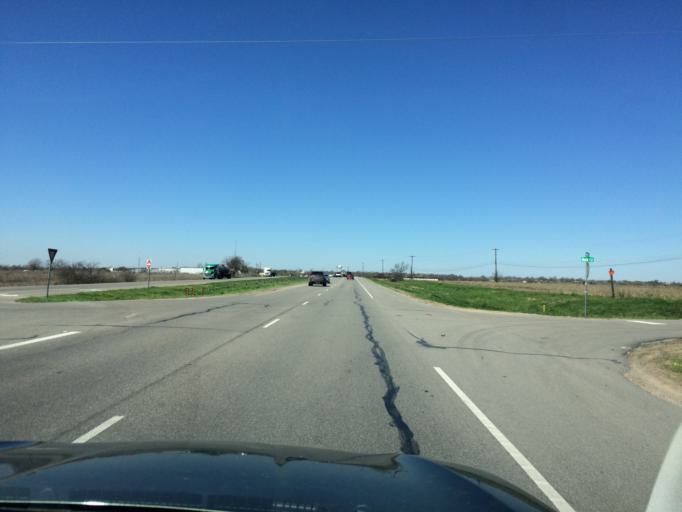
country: US
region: Texas
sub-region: Travis County
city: Garfield
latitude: 30.1825
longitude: -97.5405
